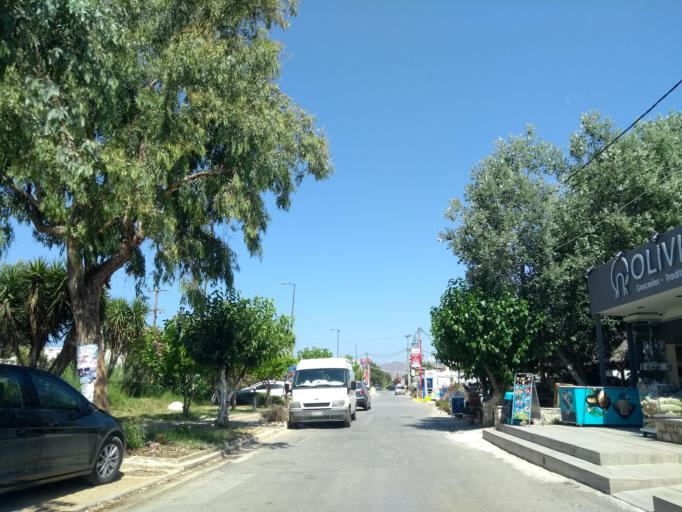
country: GR
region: Crete
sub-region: Nomos Chanias
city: Georgioupolis
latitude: 35.3510
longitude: 24.2995
